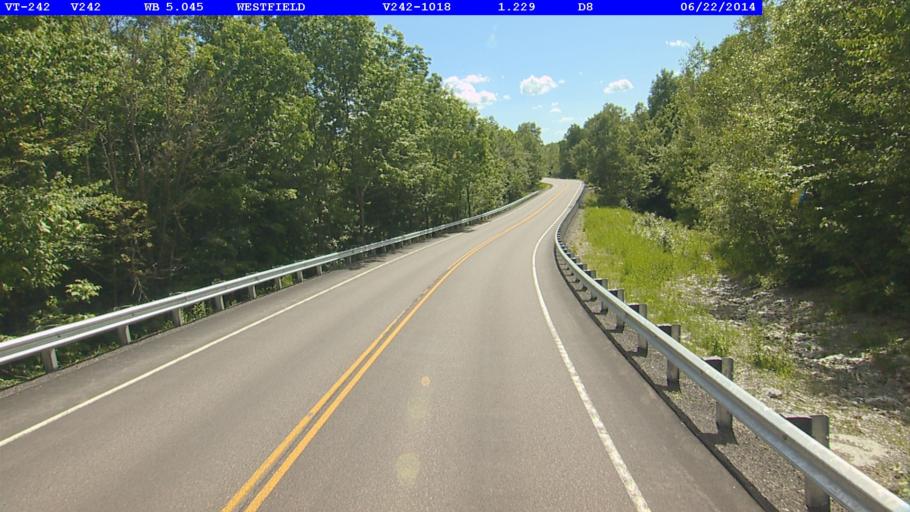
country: US
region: Vermont
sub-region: Franklin County
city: Richford
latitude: 44.8976
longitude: -72.5188
